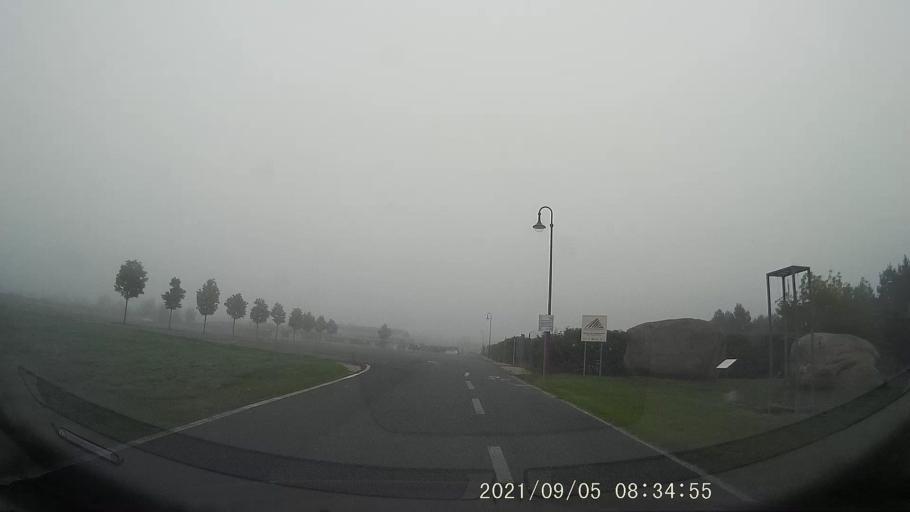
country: DE
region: Saxony
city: Boxberg
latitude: 51.4209
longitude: 14.5852
